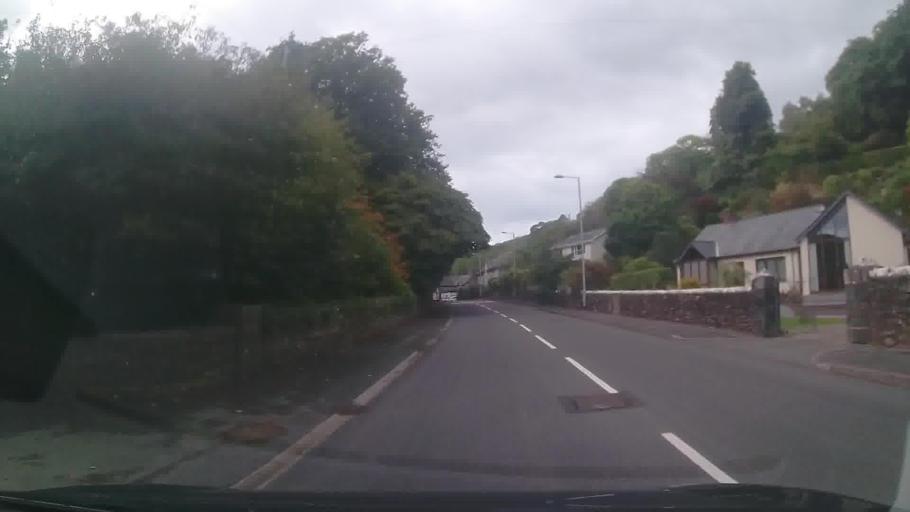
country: GB
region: Wales
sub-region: Gwynedd
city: Dolgellau
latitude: 52.7500
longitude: -3.9672
